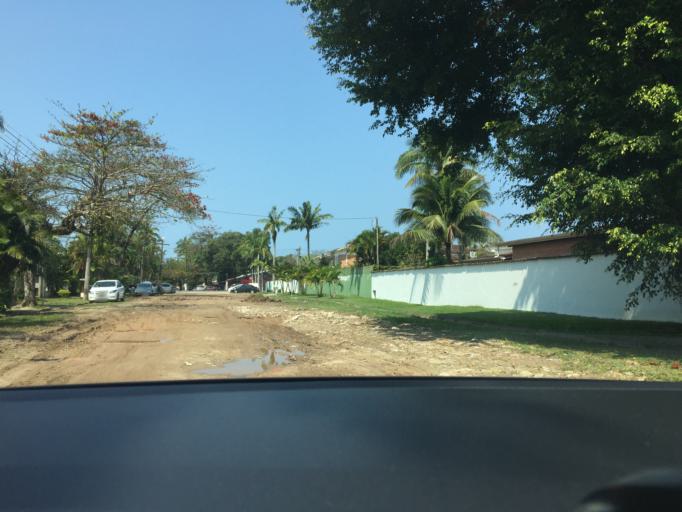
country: BR
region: Sao Paulo
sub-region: Guaruja
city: Guaruja
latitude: -23.9663
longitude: -46.1896
